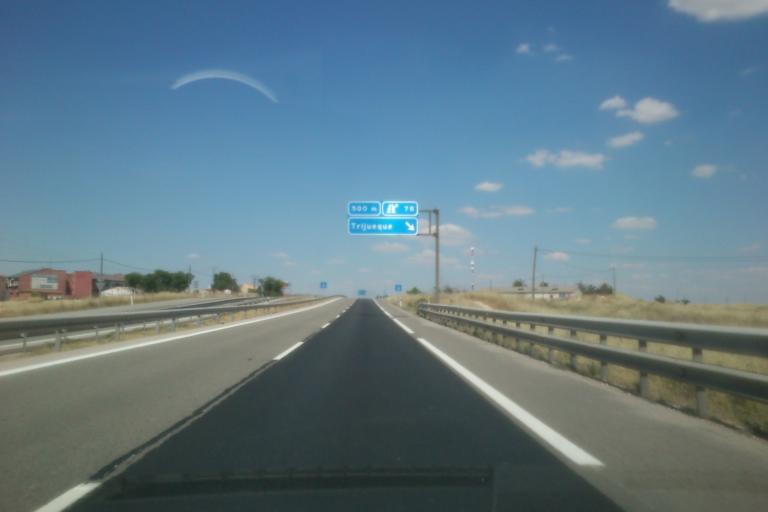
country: ES
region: Castille-La Mancha
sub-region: Provincia de Guadalajara
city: Trijueque
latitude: 40.7713
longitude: -2.9977
